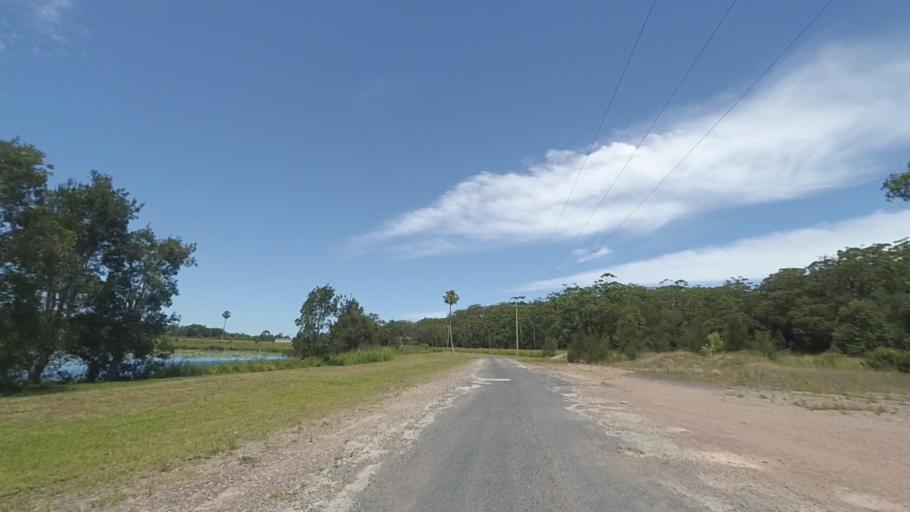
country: AU
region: New South Wales
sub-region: Port Stephens Shire
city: Anna Bay
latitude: -32.7708
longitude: 151.9997
